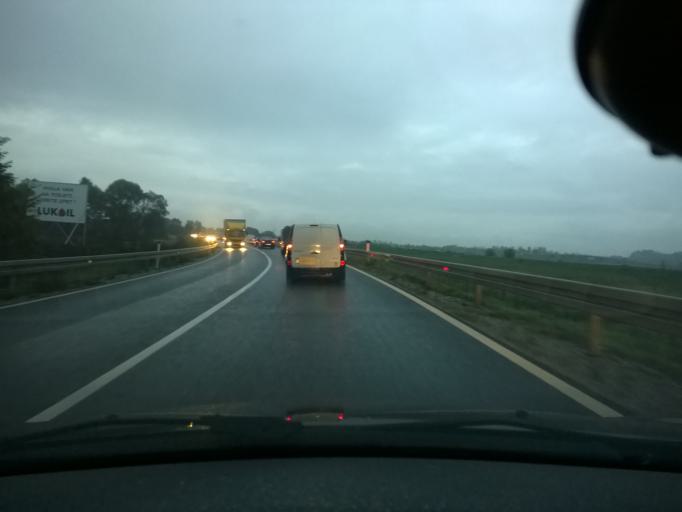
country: HR
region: Zagrebacka
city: Pojatno
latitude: 45.8843
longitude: 15.8191
